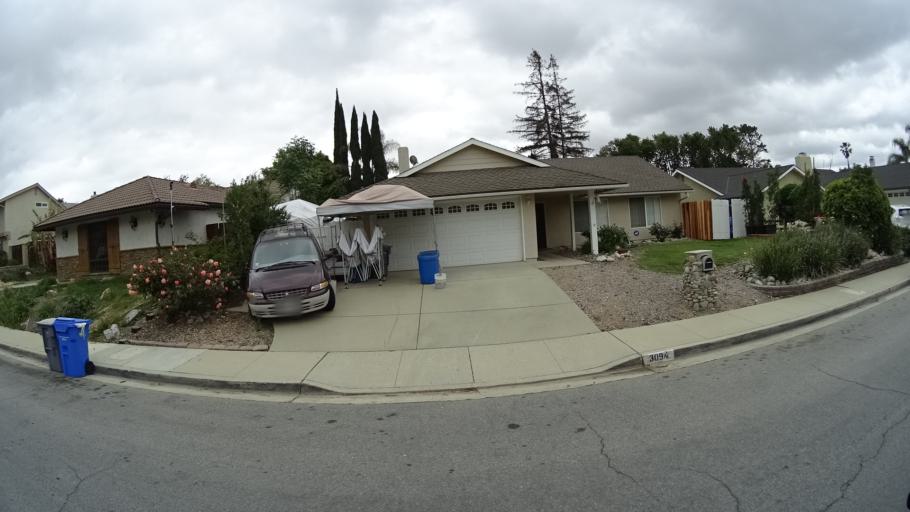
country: US
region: California
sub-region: Ventura County
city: Casa Conejo
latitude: 34.2217
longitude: -118.9011
